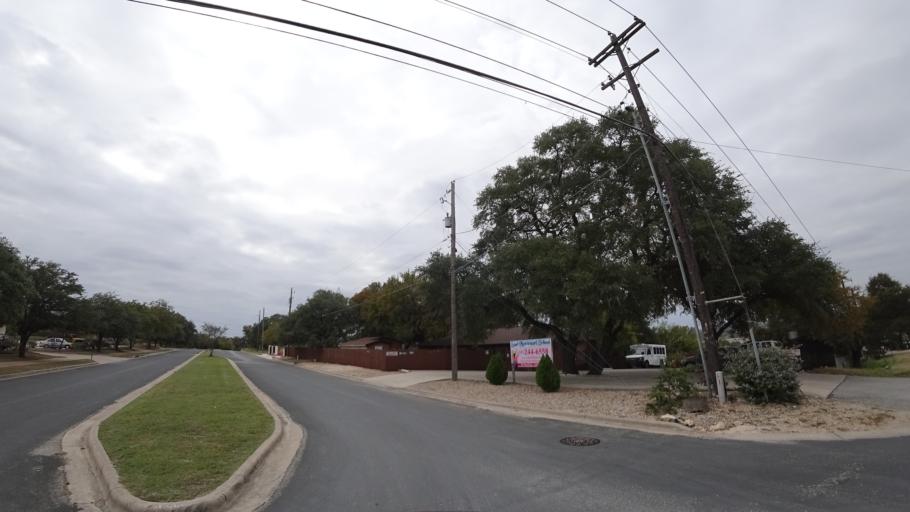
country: US
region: Texas
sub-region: Travis County
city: Wells Branch
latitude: 30.4386
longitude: -97.6946
